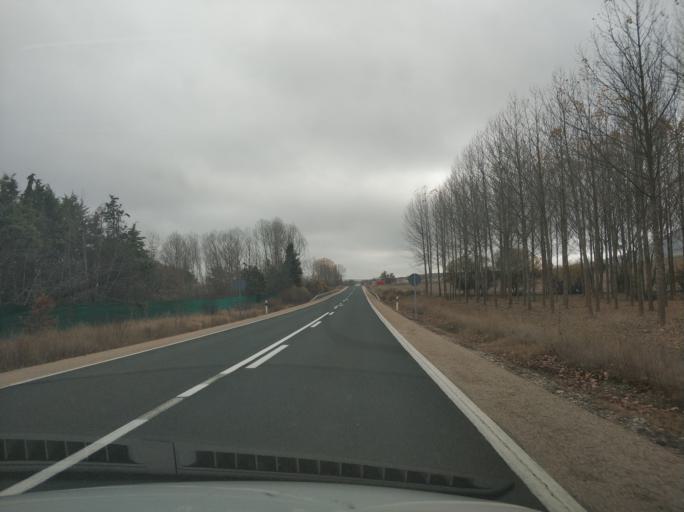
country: ES
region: Castille and Leon
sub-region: Provincia de Soria
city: Cidones
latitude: 41.8052
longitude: -2.5804
